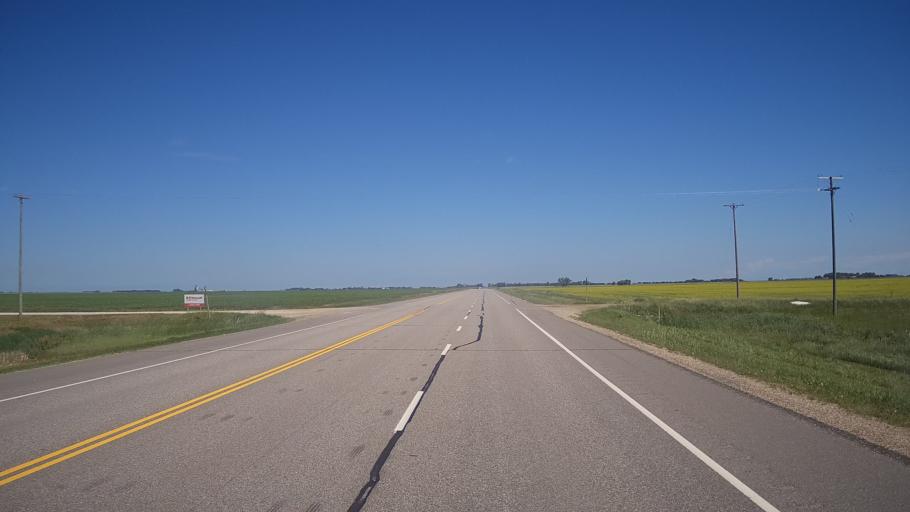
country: CA
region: Manitoba
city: Portage la Prairie
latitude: 50.0187
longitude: -98.4688
